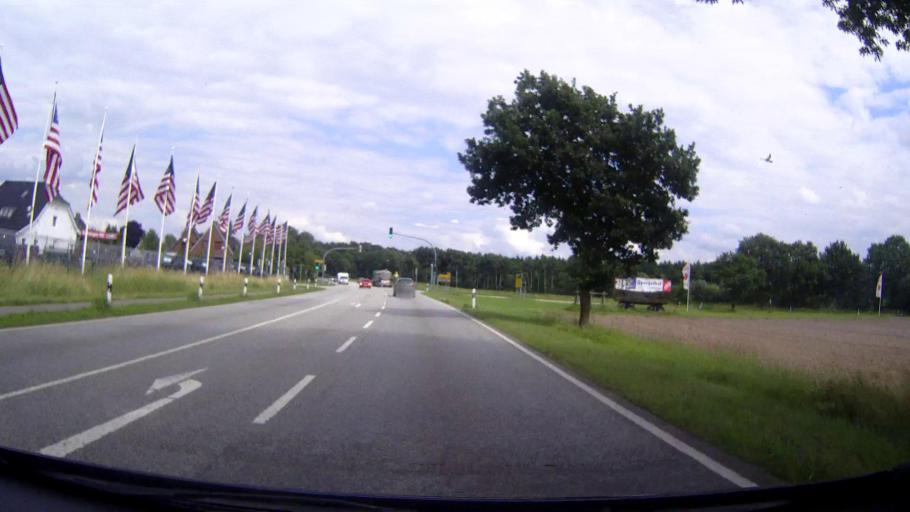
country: DE
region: Schleswig-Holstein
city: Wasbek
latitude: 54.0684
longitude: 9.8931
